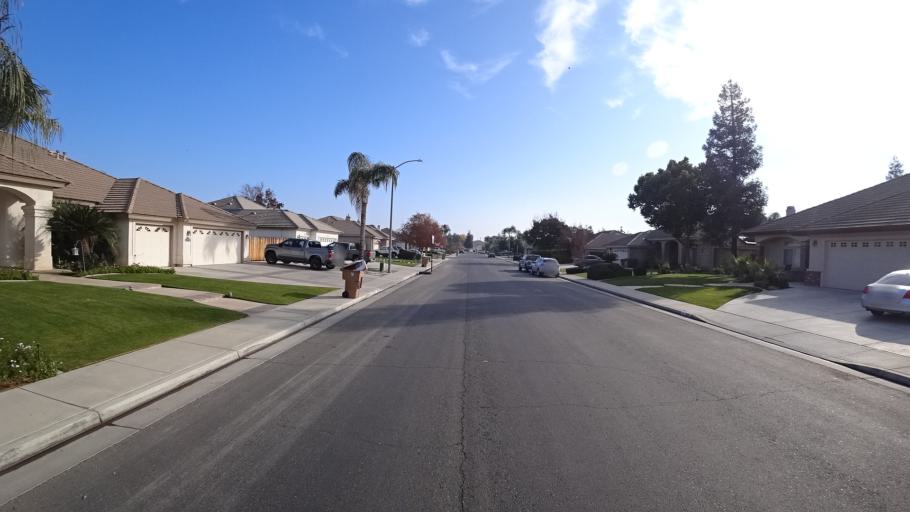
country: US
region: California
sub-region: Kern County
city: Rosedale
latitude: 35.3664
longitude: -119.1577
